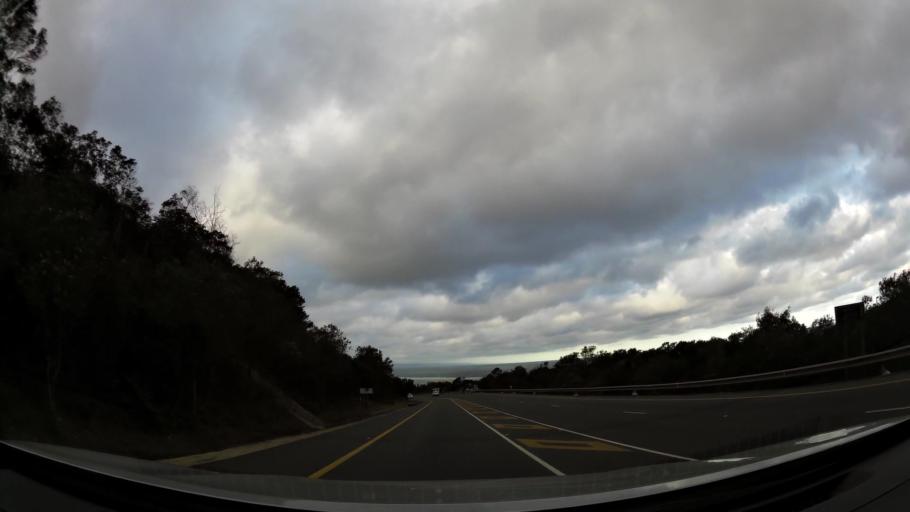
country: ZA
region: Western Cape
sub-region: Eden District Municipality
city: Plettenberg Bay
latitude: -34.0442
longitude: 23.3649
